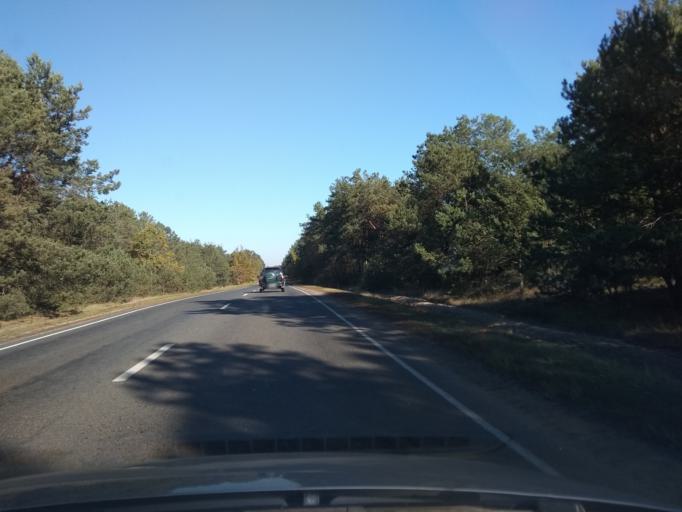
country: BY
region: Brest
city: Kobryn
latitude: 52.1367
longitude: 24.3087
